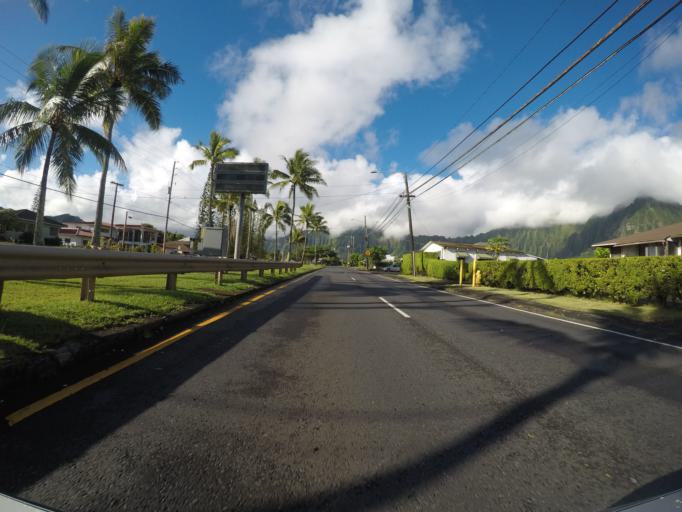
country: US
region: Hawaii
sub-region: Honolulu County
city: Kane'ohe
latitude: 21.4085
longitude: -157.7994
